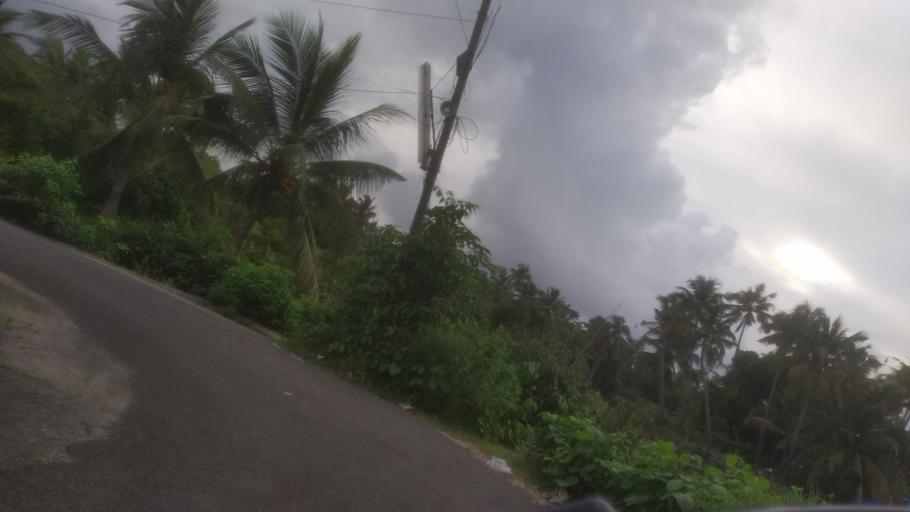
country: IN
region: Kerala
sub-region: Ernakulam
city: Elur
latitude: 10.0967
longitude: 76.2105
